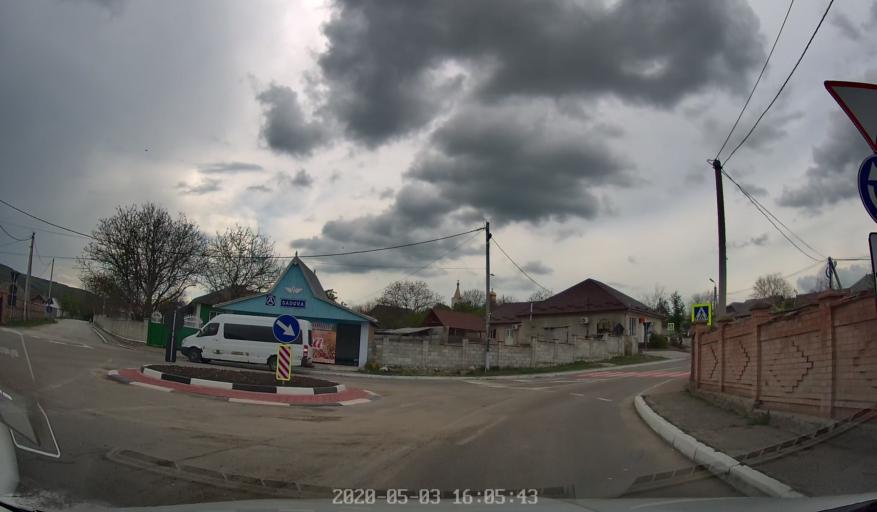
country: MD
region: Calarasi
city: Calarasi
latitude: 47.1906
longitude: 28.3548
